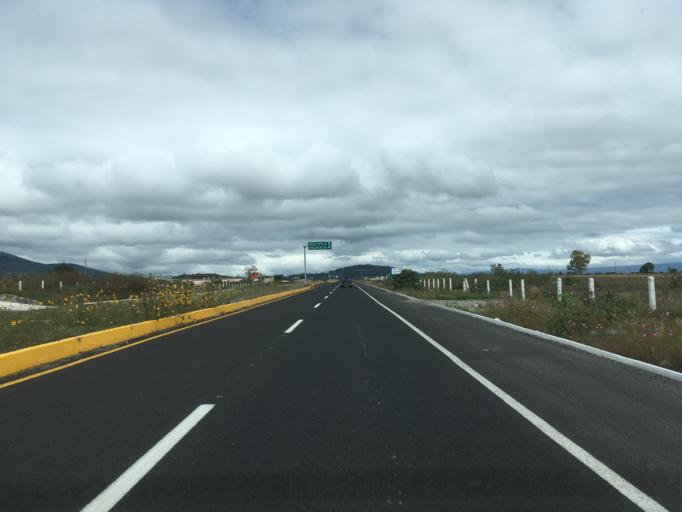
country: MX
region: Hidalgo
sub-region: Atotonilco el Grande
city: Santa Maria Amajac
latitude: 20.3668
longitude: -98.7210
